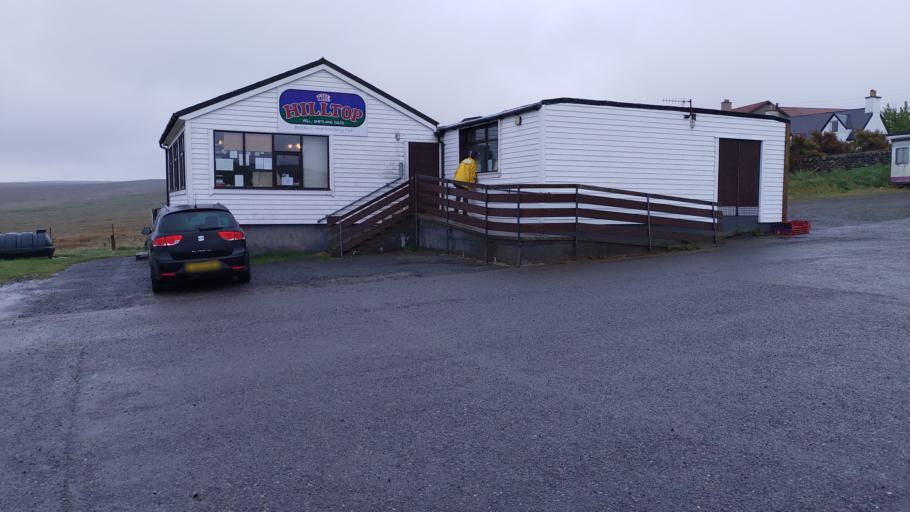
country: GB
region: Scotland
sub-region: Shetland Islands
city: Shetland
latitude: 60.5977
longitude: -1.0658
